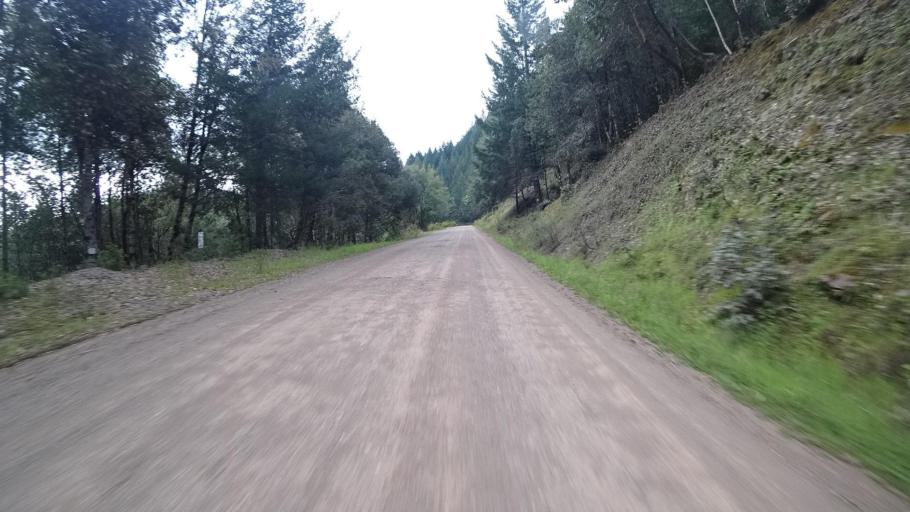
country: US
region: California
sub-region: Humboldt County
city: Redway
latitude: 40.2254
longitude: -123.7612
